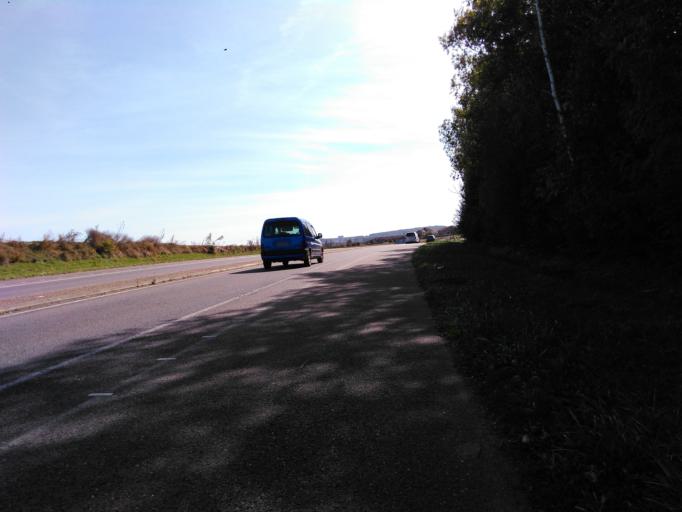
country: FR
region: Lorraine
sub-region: Departement de la Moselle
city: Thionville
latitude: 49.3903
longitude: 6.1685
